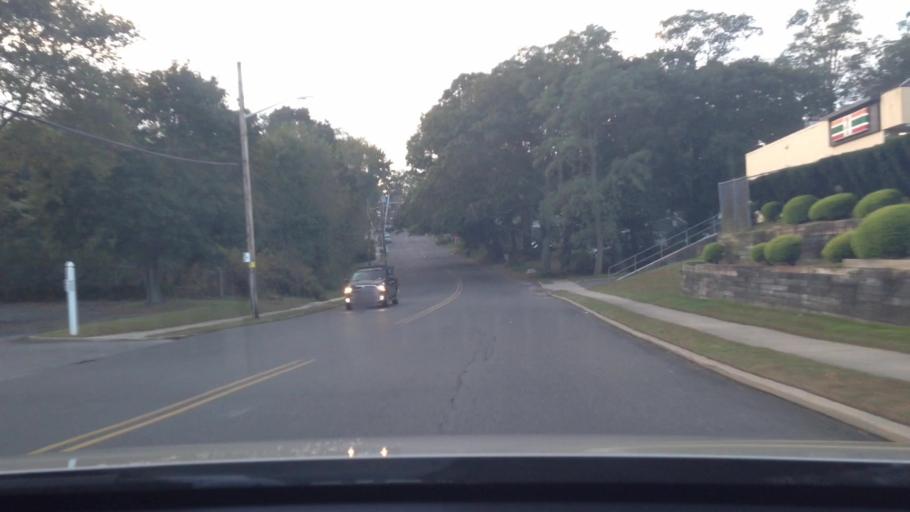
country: US
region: New York
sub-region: Suffolk County
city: Selden
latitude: 40.8660
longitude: -73.0354
